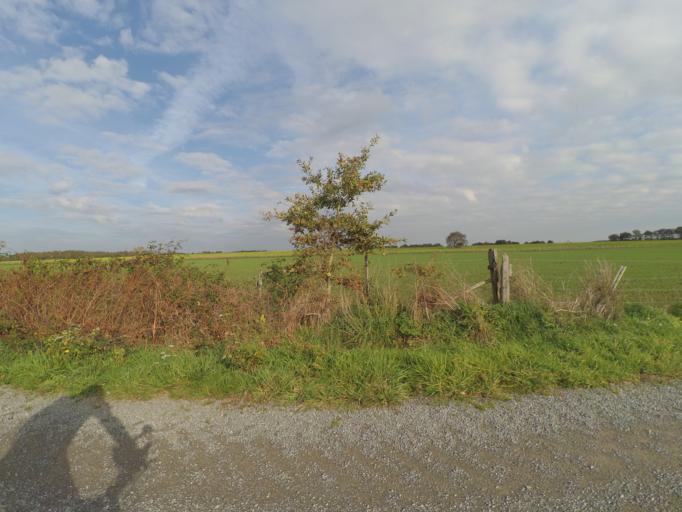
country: FR
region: Pays de la Loire
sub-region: Departement de la Loire-Atlantique
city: La Planche
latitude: 46.9927
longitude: -1.3899
